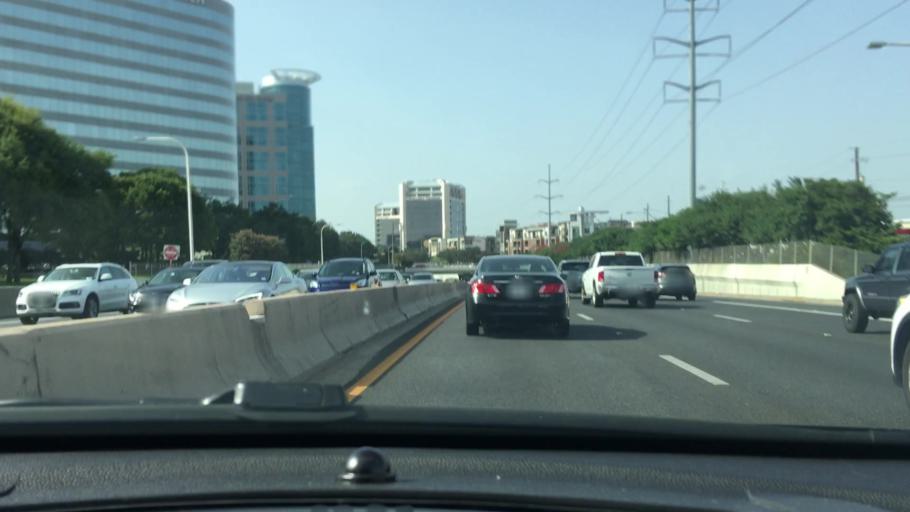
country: US
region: Texas
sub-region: Dallas County
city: Addison
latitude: 32.9572
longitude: -96.8215
